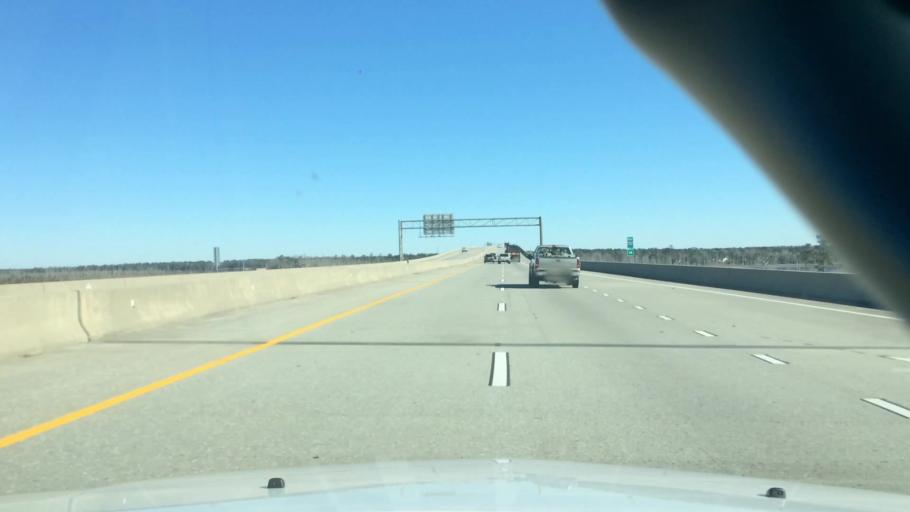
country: US
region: North Carolina
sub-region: New Hanover County
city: Wrightsboro
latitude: 34.2943
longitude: -77.9638
